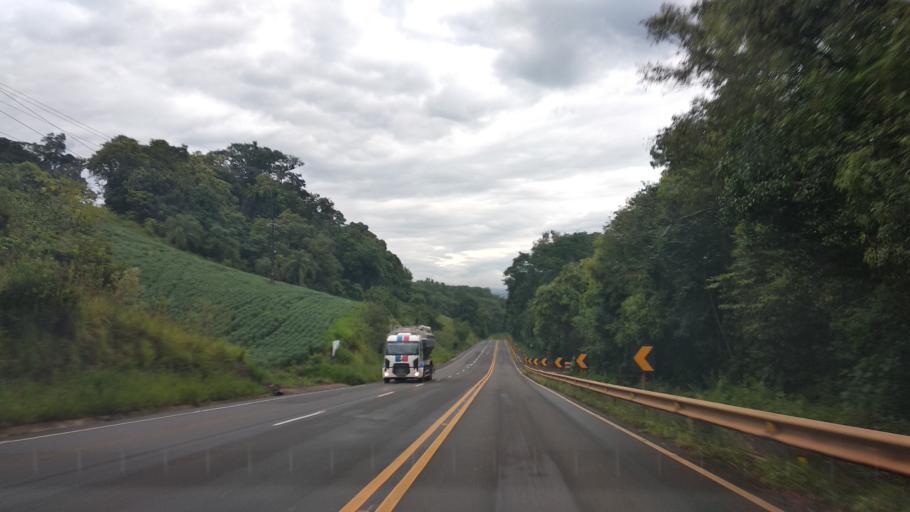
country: BR
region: Santa Catarina
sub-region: Videira
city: Videira
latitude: -27.0853
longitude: -51.2403
